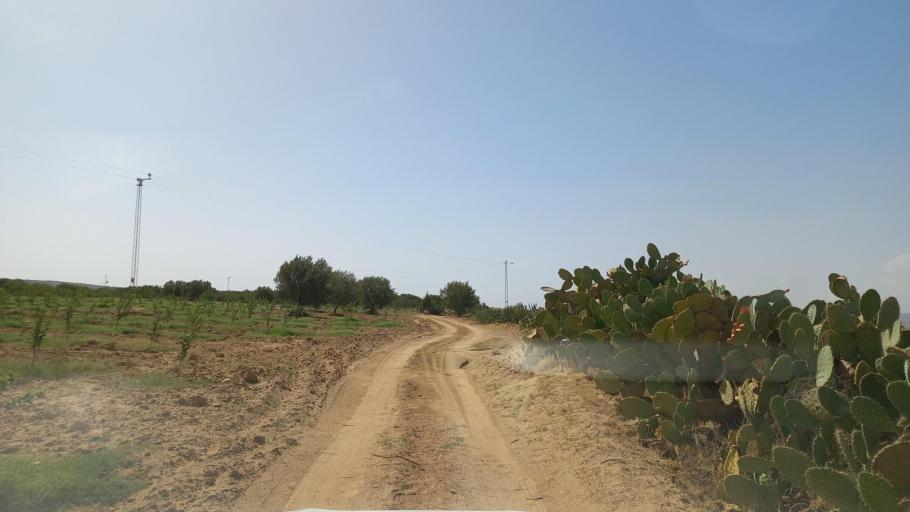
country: TN
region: Al Qasrayn
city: Kasserine
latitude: 35.2136
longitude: 9.0325
